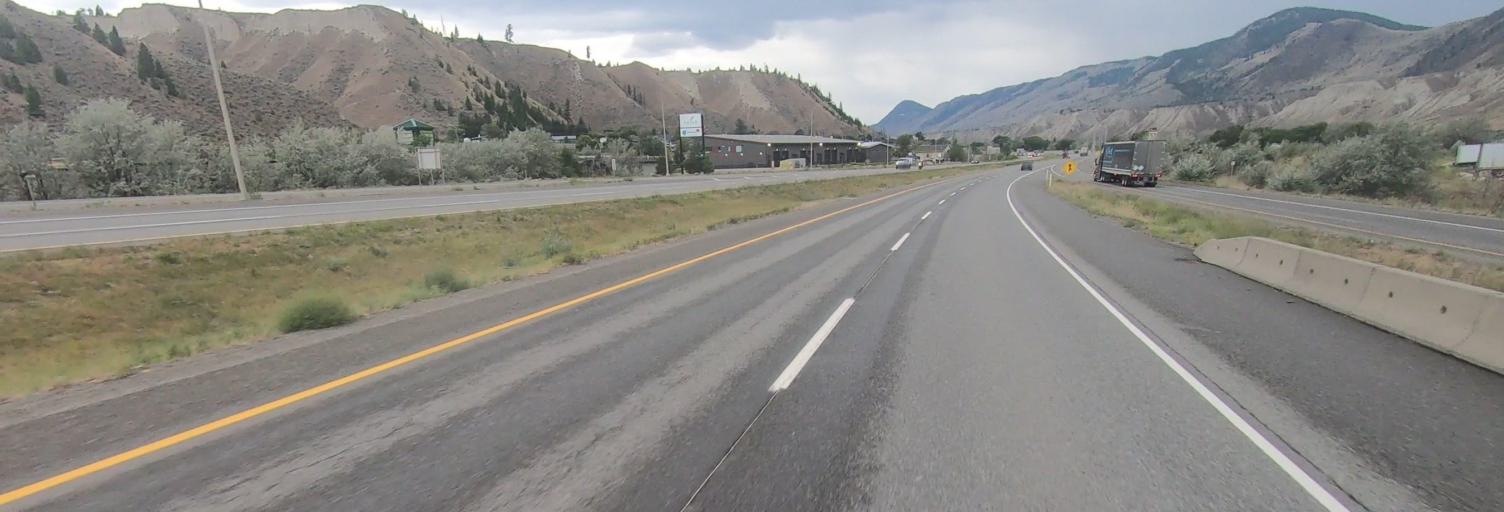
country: CA
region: British Columbia
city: Kamloops
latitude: 50.6602
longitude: -120.1223
